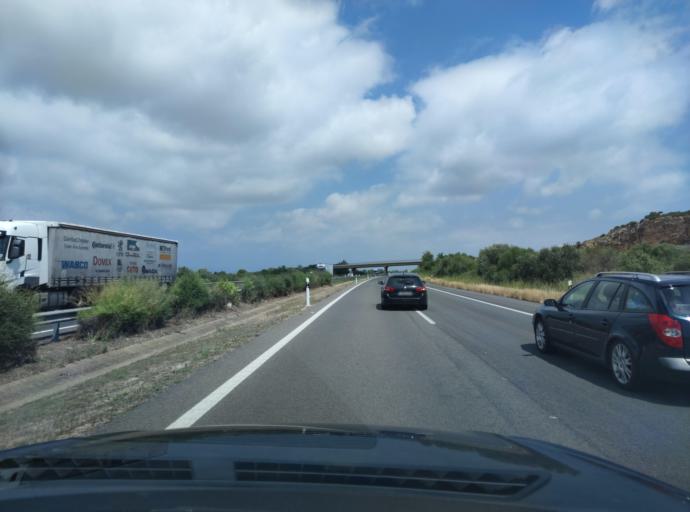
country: ES
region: Valencia
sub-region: Provincia de Castello
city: Vinaros
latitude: 40.4882
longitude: 0.4154
